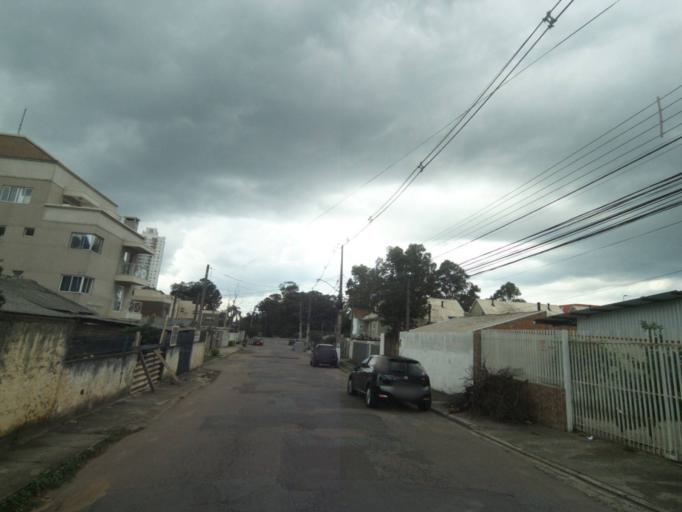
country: BR
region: Parana
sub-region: Curitiba
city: Curitiba
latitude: -25.4461
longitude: -49.3520
